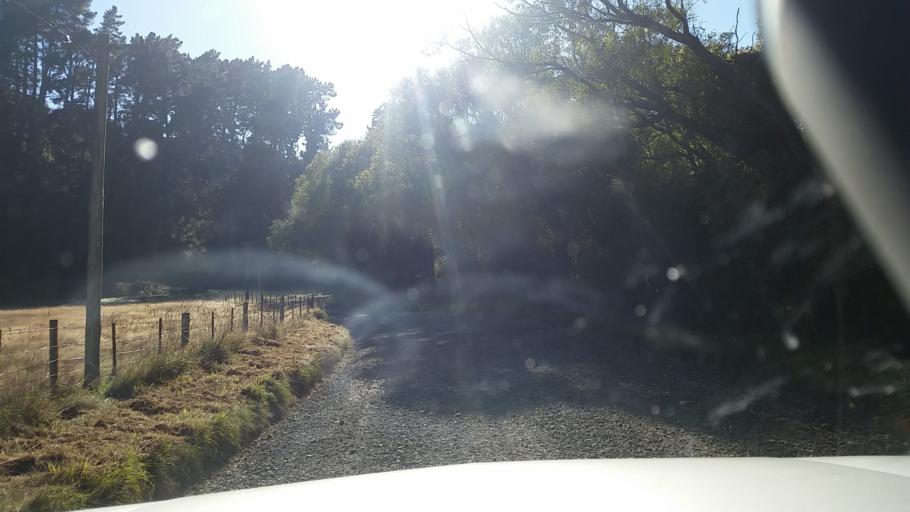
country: NZ
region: Marlborough
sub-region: Marlborough District
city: Blenheim
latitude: -41.4512
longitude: 173.8718
